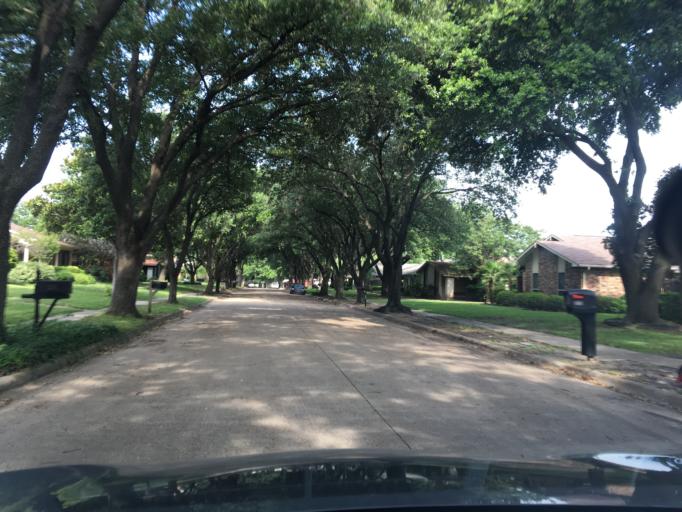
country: US
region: Texas
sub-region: Collin County
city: Plano
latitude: 32.9690
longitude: -96.6784
